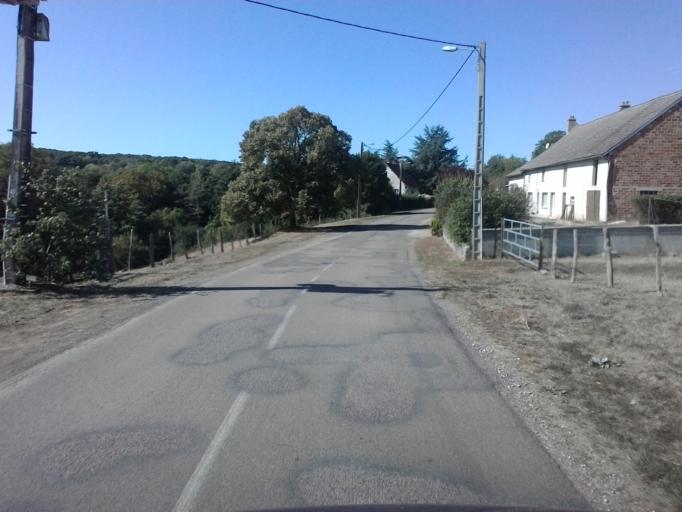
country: FR
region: Bourgogne
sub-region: Departement de la Cote-d'Or
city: Semur-en-Auxois
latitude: 47.4731
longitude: 4.3601
